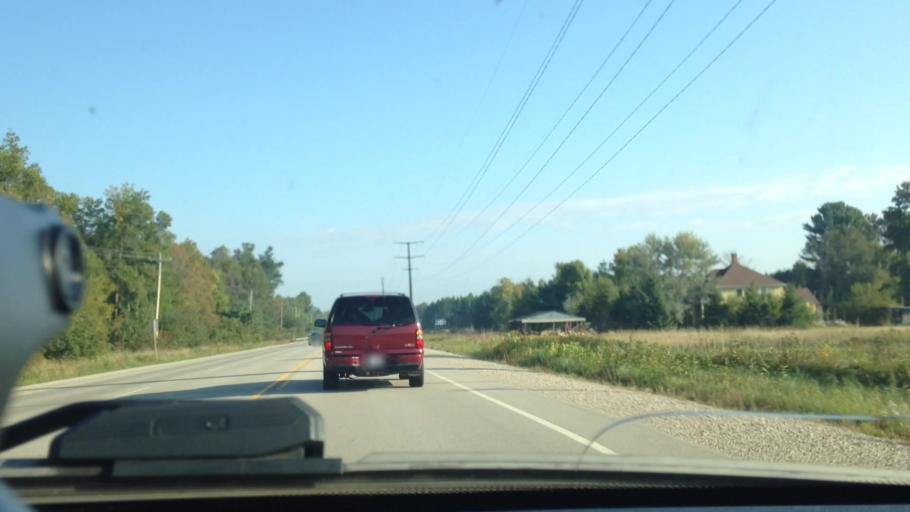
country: US
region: Wisconsin
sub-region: Marinette County
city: Peshtigo
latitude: 45.1834
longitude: -87.9955
